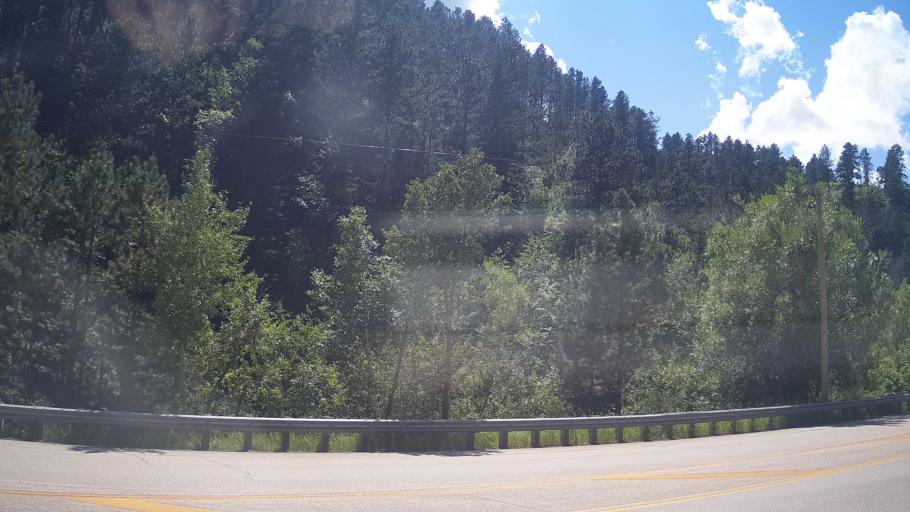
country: US
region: South Dakota
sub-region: Lawrence County
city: Deadwood
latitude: 44.3709
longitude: -103.7441
